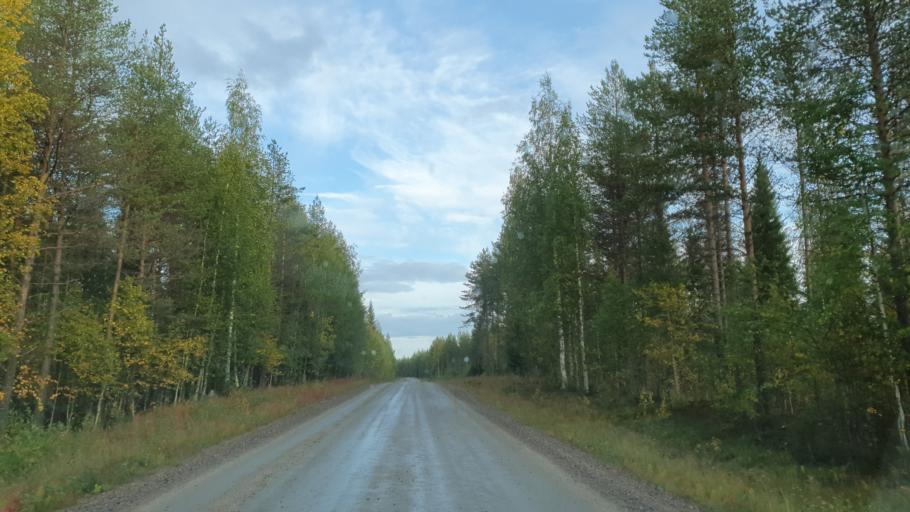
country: FI
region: Kainuu
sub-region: Kehys-Kainuu
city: Kuhmo
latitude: 64.4177
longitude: 29.4997
